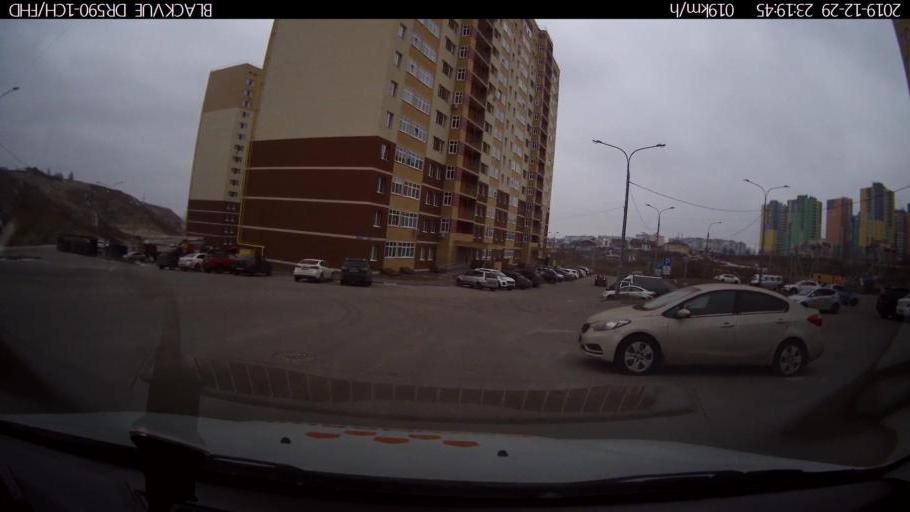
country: RU
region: Nizjnij Novgorod
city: Afonino
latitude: 56.2811
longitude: 44.0888
